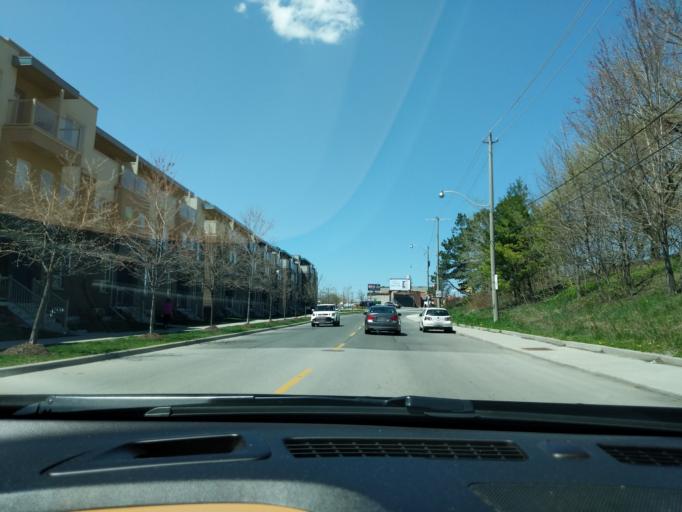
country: CA
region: Ontario
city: Toronto
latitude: 43.6738
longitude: -79.4537
